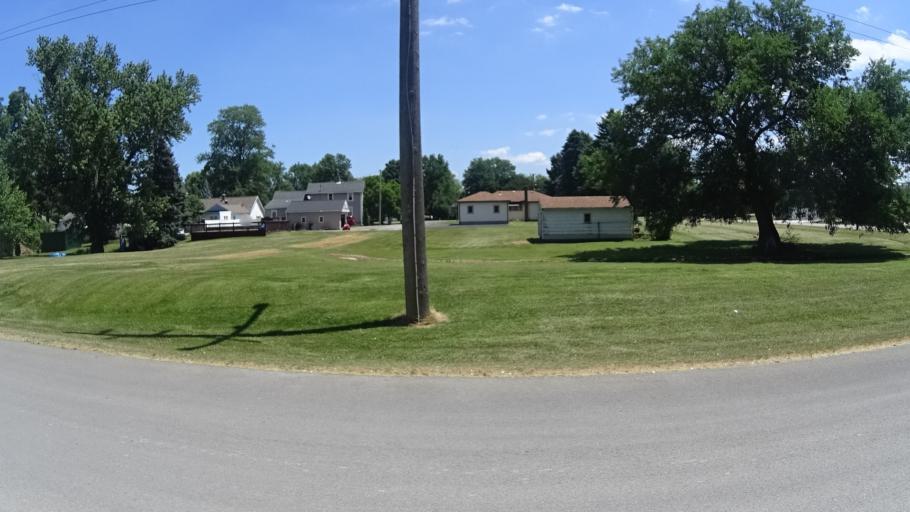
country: US
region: Ohio
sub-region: Erie County
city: Huron
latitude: 41.3903
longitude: -82.5471
